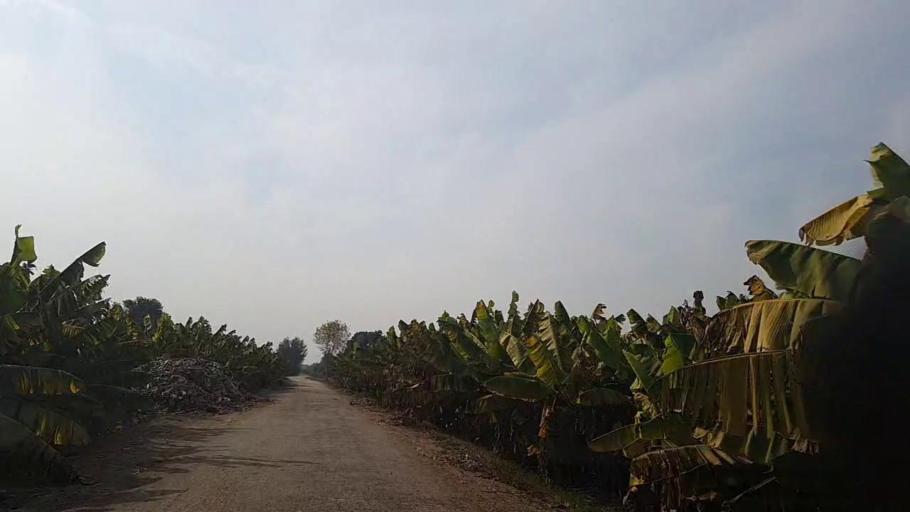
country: PK
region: Sindh
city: Daur
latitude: 26.3995
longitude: 68.2064
